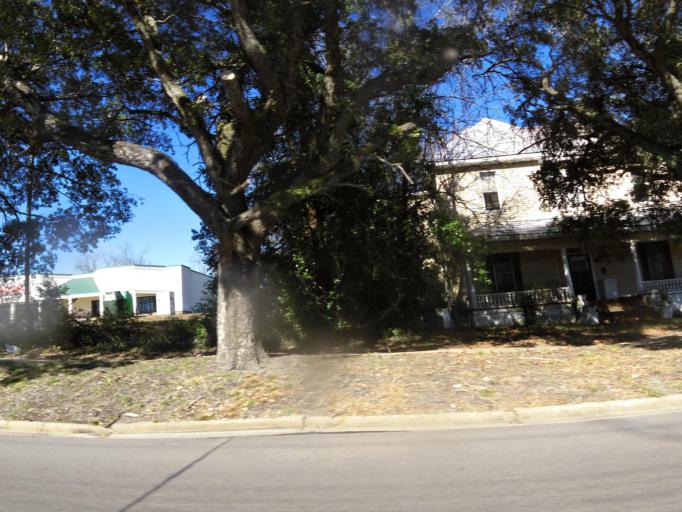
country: US
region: Alabama
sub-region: Bullock County
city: Union Springs
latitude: 32.1463
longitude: -85.7114
